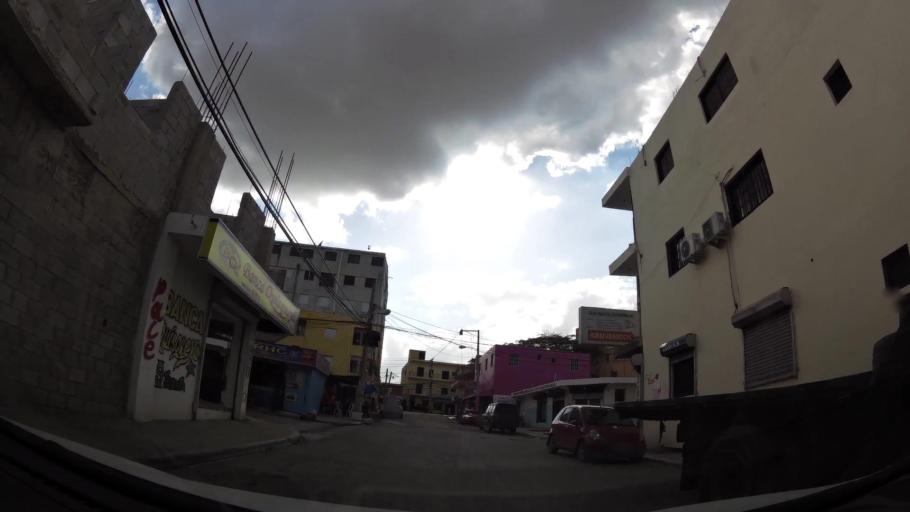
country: DO
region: Nacional
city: Ensanche Luperon
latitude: 18.5581
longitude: -69.9038
